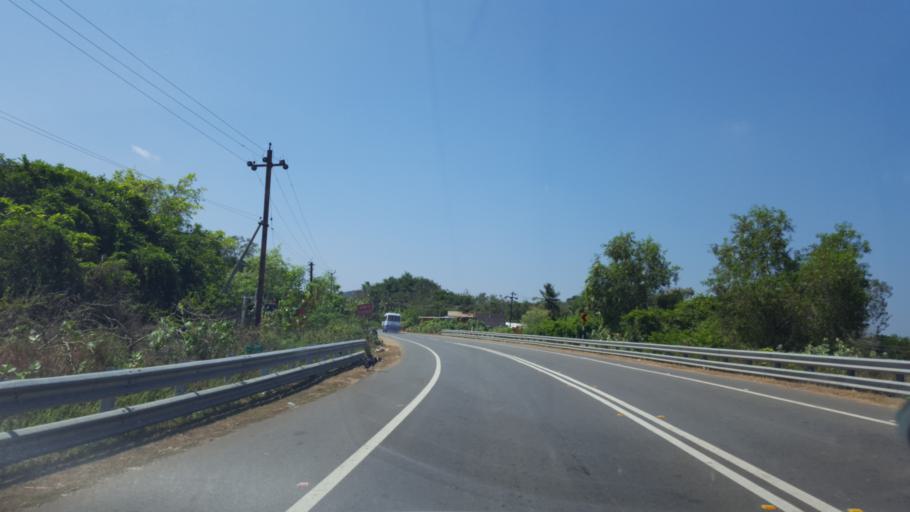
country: IN
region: Tamil Nadu
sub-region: Kancheepuram
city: Karumbakkam
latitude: 12.6231
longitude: 80.0605
